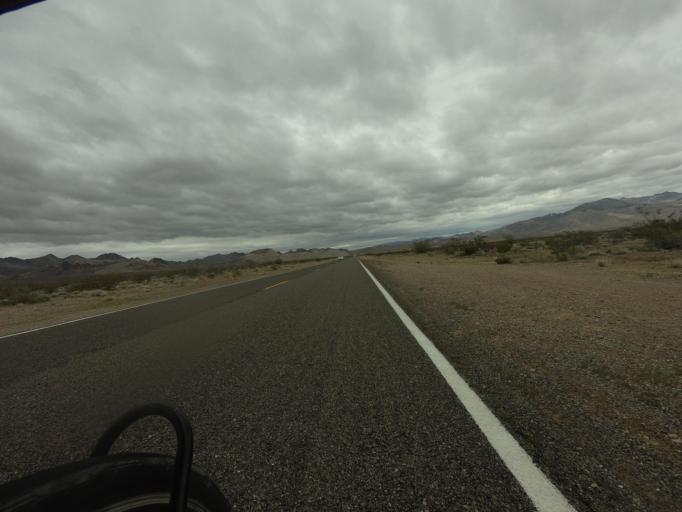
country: US
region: Nevada
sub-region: Nye County
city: Beatty
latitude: 36.8609
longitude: -116.8435
